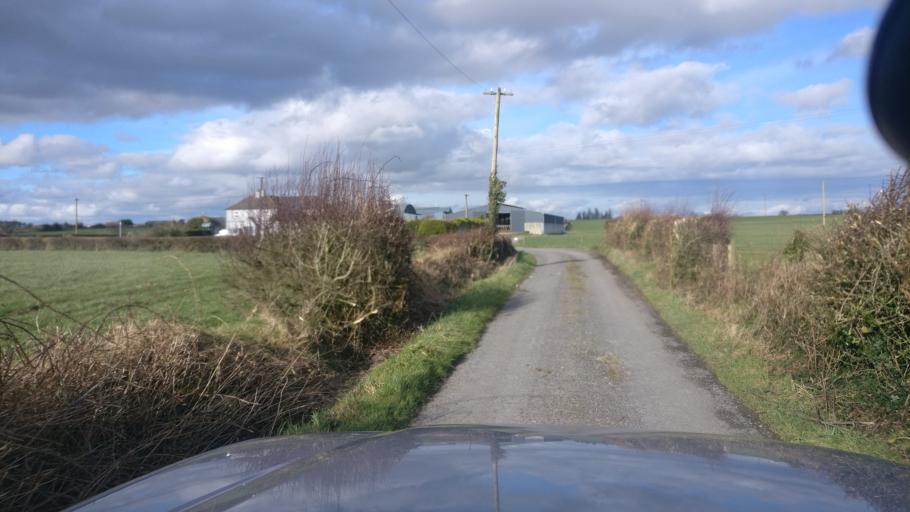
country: IE
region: Connaught
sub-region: County Galway
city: Loughrea
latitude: 53.2070
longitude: -8.4216
